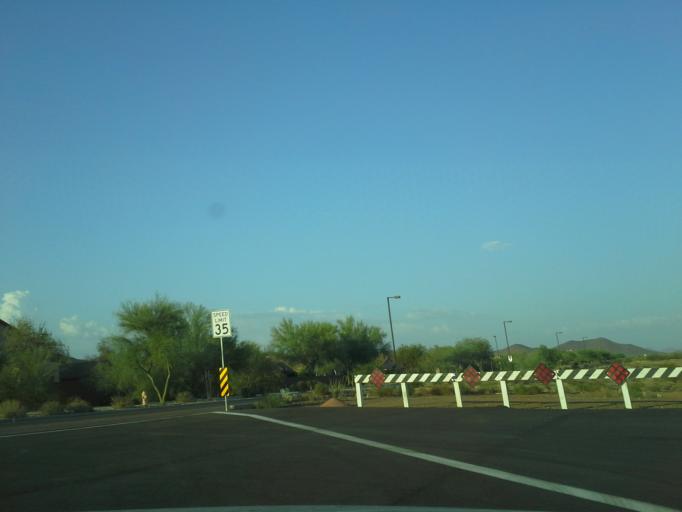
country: US
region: Arizona
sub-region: Maricopa County
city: Anthem
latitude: 33.7692
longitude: -112.1090
